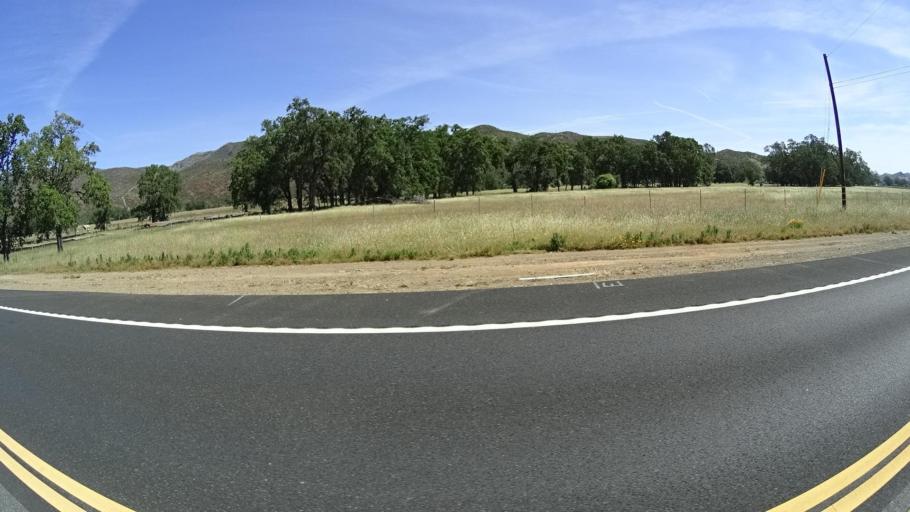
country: US
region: California
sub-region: Lake County
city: Middletown
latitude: 38.7646
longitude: -122.6473
